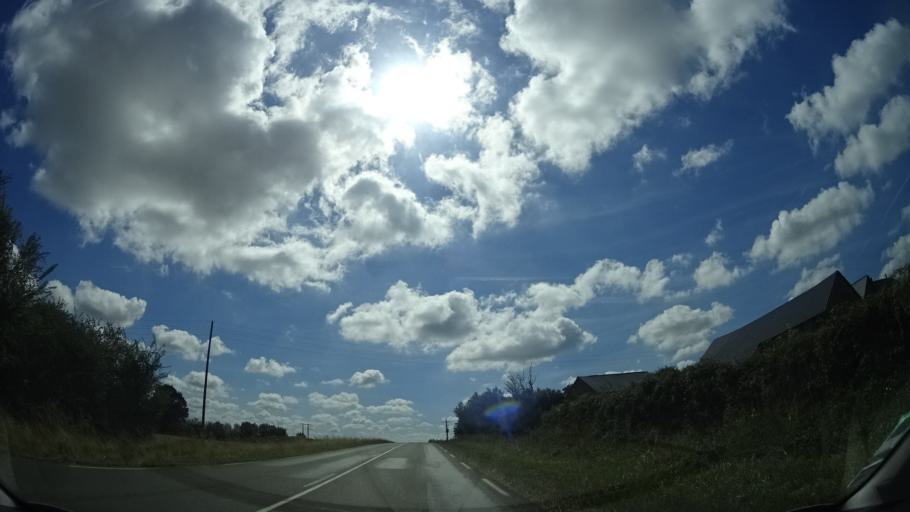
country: FR
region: Pays de la Loire
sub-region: Departement de la Mayenne
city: Meslay-du-Maine
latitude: 47.9291
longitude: -0.4933
